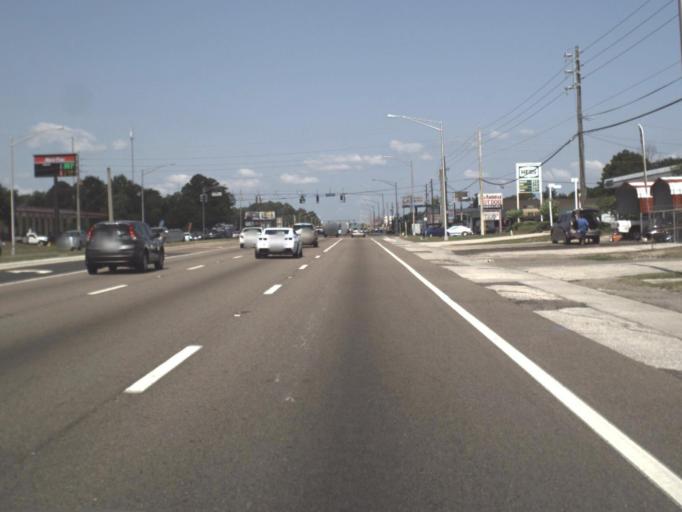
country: US
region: Florida
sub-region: Duval County
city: Jacksonville
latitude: 30.2868
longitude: -81.5427
